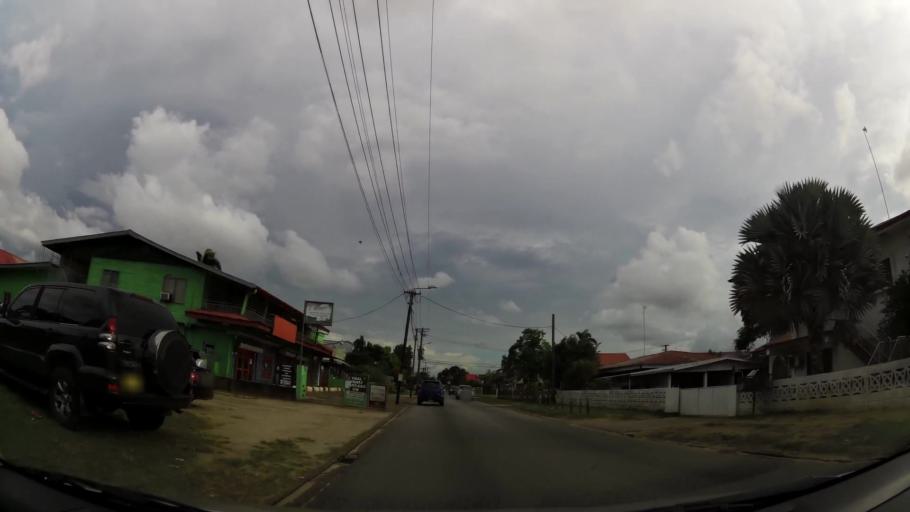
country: SR
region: Paramaribo
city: Paramaribo
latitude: 5.8445
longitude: -55.1843
